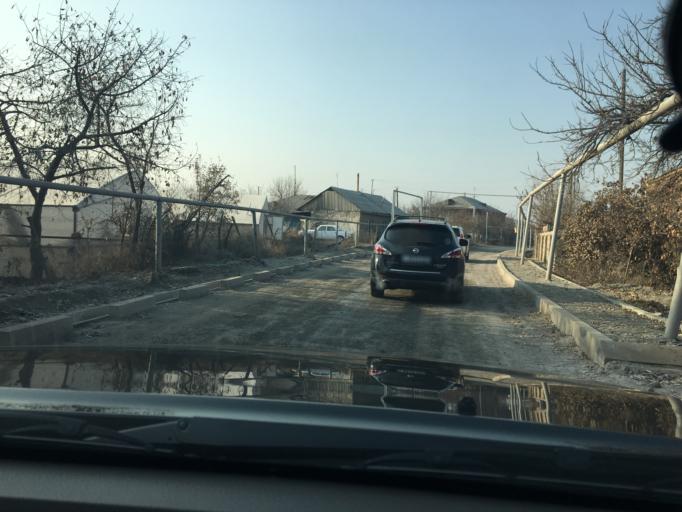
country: AM
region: Armavir
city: Janfida
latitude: 40.0443
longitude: 44.0285
